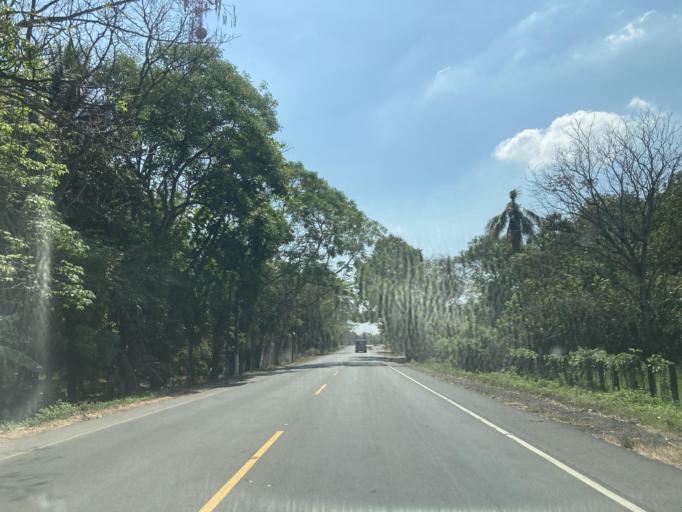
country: GT
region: Escuintla
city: Guanagazapa
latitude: 14.2076
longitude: -90.7178
